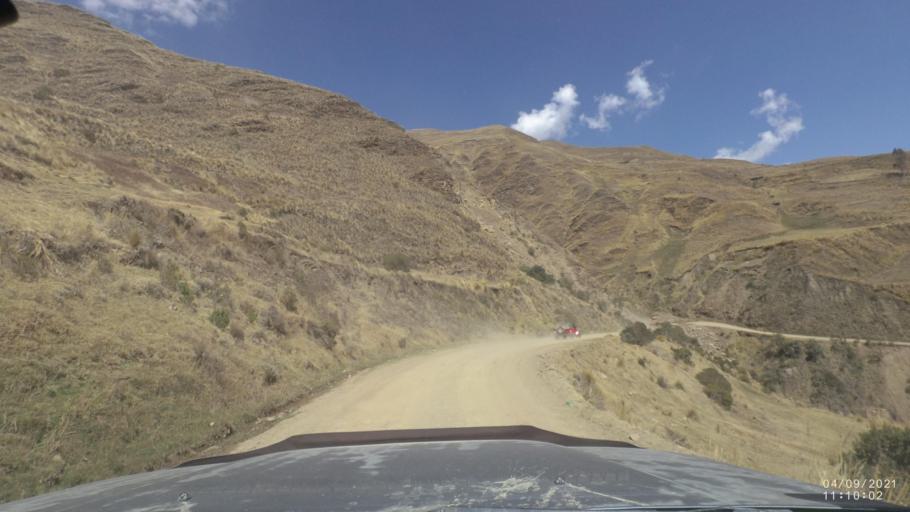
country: BO
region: Cochabamba
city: Sipe Sipe
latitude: -17.2782
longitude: -66.4807
